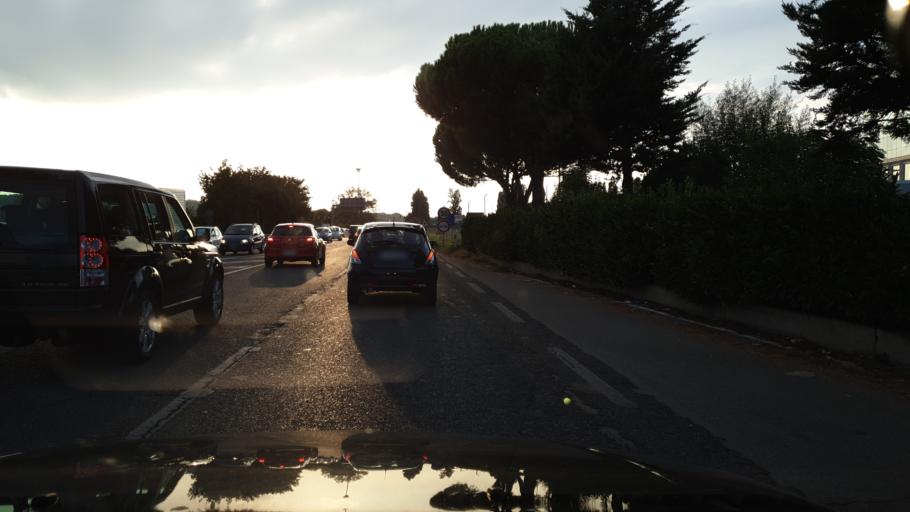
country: IT
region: Emilia-Romagna
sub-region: Provincia di Rimini
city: Rimini
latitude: 44.0419
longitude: 12.5753
